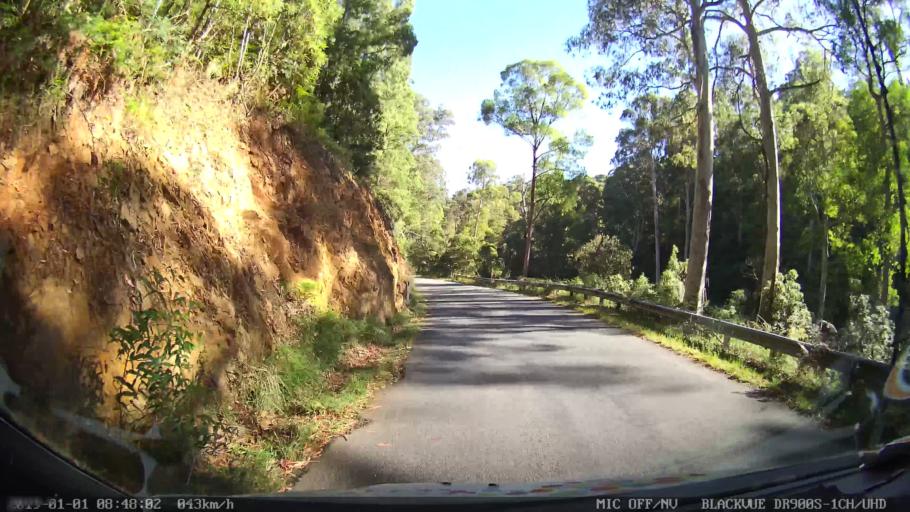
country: AU
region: New South Wales
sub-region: Snowy River
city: Jindabyne
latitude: -36.2912
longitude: 148.1992
